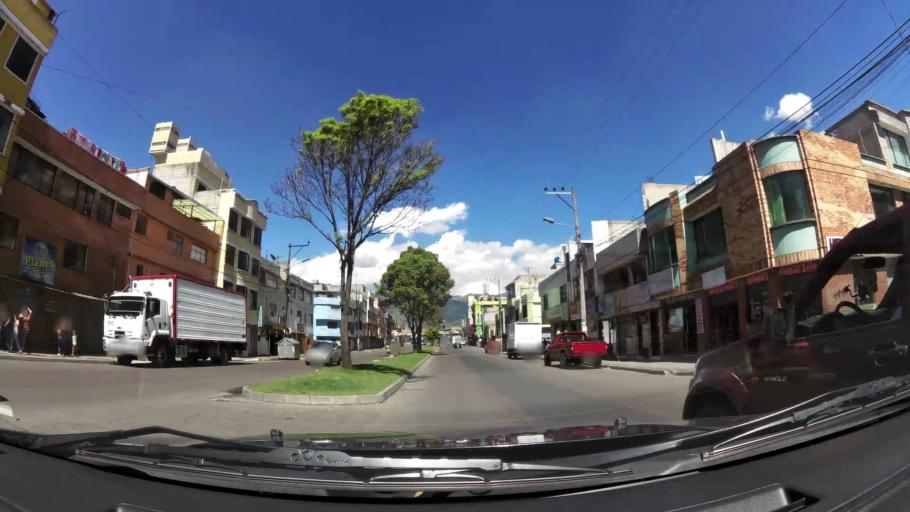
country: EC
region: Pichincha
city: Quito
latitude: -0.2674
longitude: -78.5454
